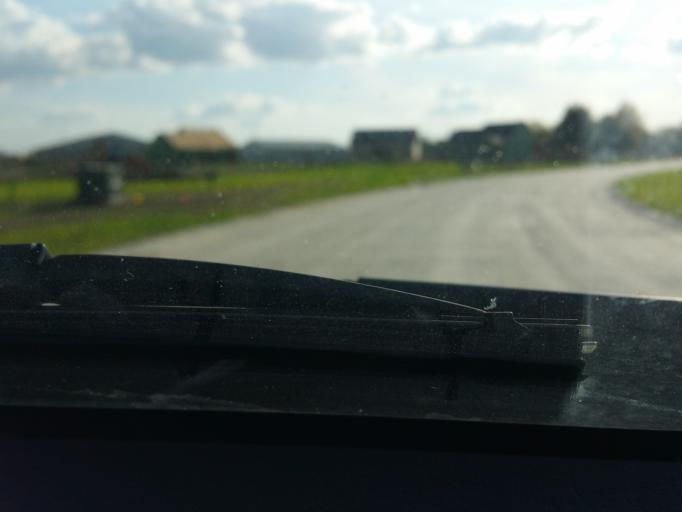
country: US
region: Illinois
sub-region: Madison County
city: Edwardsville
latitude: 38.7900
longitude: -89.9615
